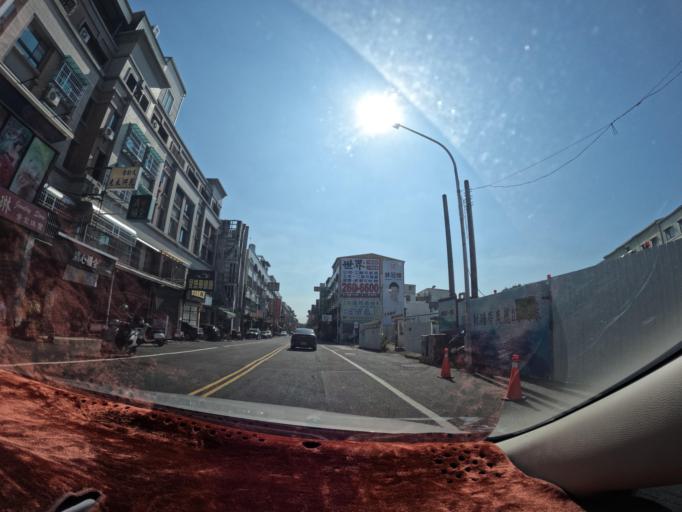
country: TW
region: Taiwan
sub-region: Tainan
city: Tainan
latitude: 23.0171
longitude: 120.2436
